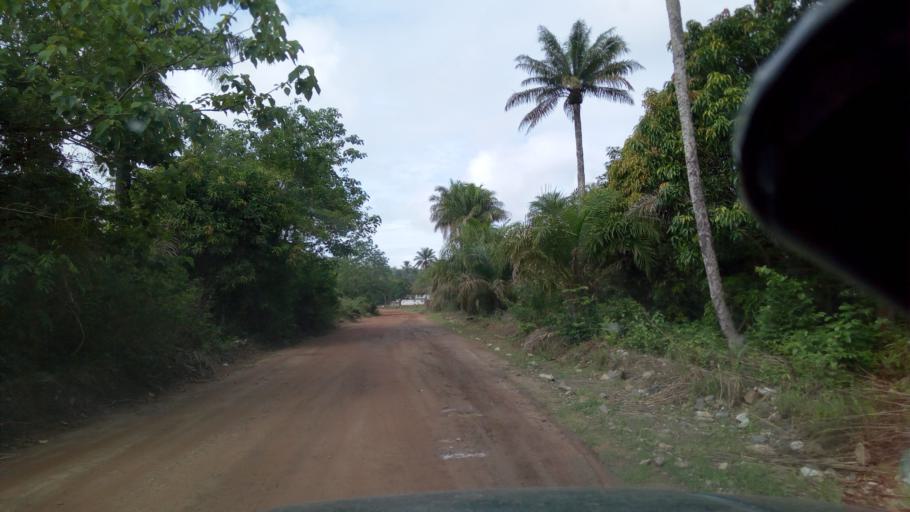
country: SL
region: Northern Province
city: Pepel
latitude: 8.6335
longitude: -13.0296
